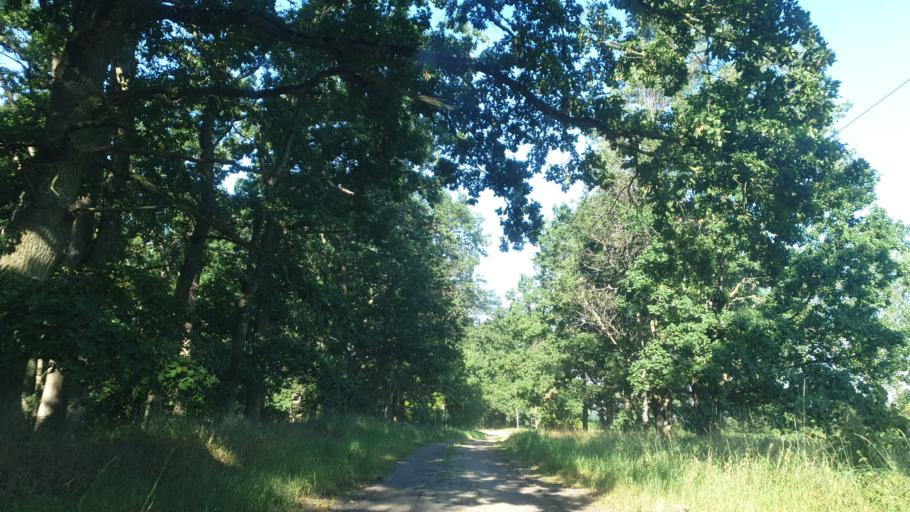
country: DE
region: Mecklenburg-Vorpommern
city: Ferdinandshof
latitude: 53.6542
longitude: 13.9501
